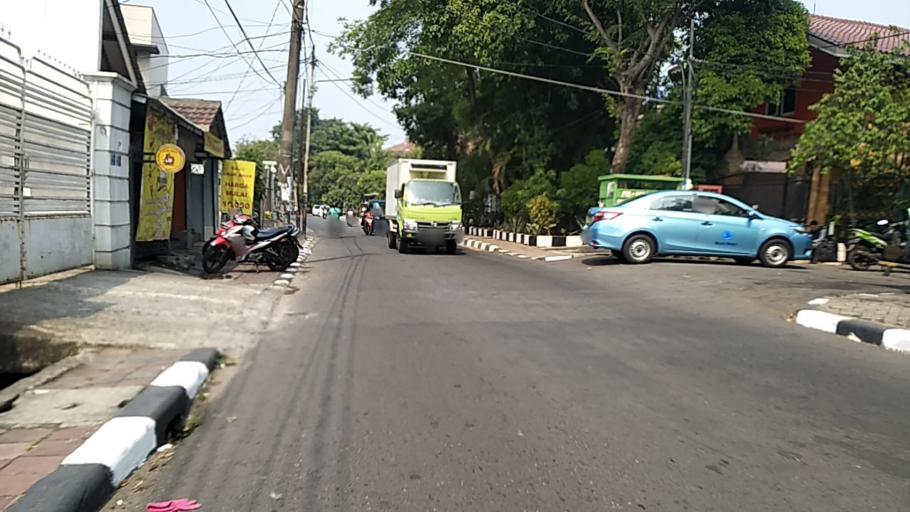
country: ID
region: Jakarta Raya
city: Jakarta
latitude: -6.2322
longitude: 106.8492
